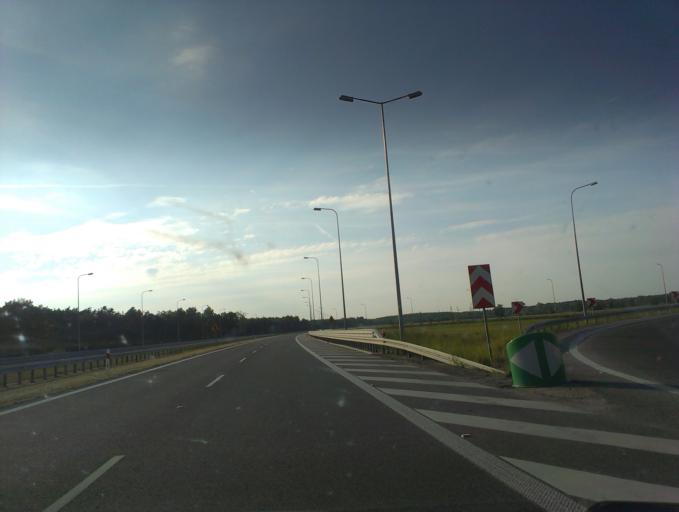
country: PL
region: Greater Poland Voivodeship
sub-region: Powiat rawicki
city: Rawicz
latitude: 51.6076
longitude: 16.8050
